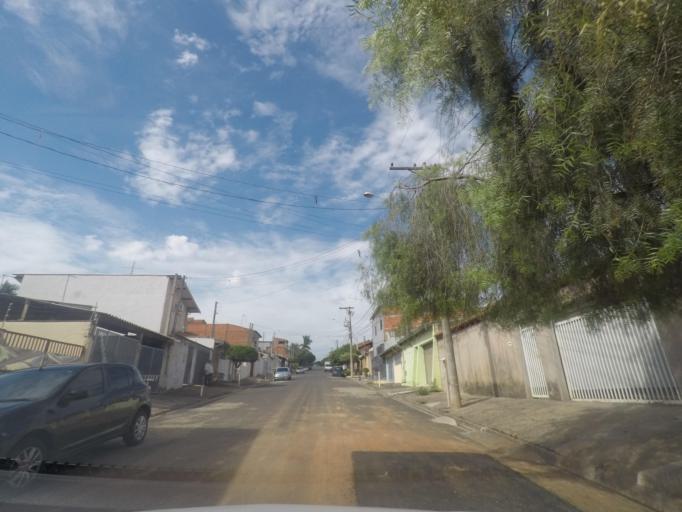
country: BR
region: Sao Paulo
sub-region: Sumare
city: Sumare
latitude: -22.8067
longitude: -47.2722
